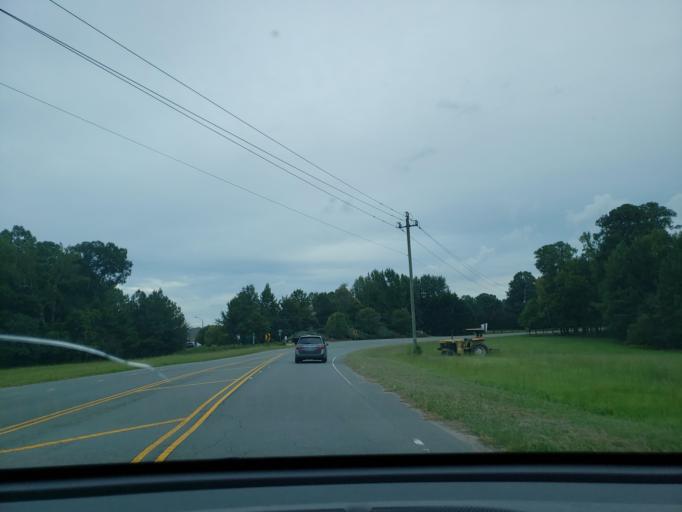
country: US
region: North Carolina
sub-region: Wake County
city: Morrisville
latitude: 35.7924
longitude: -78.8579
